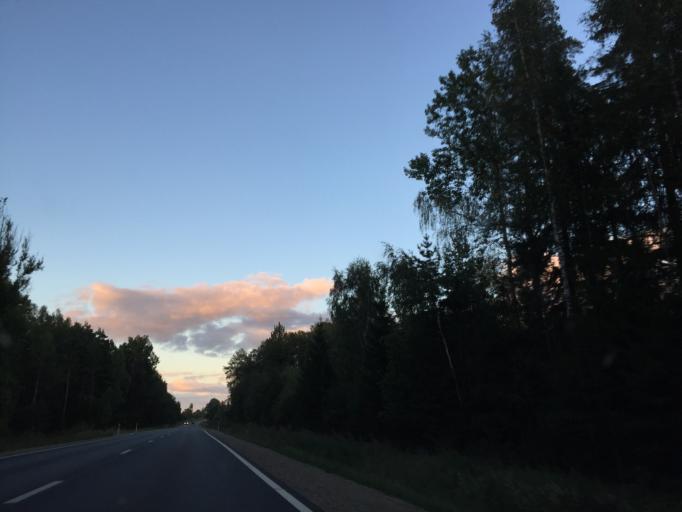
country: LV
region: Jaunpils
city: Jaunpils
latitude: 56.6967
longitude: 23.1447
